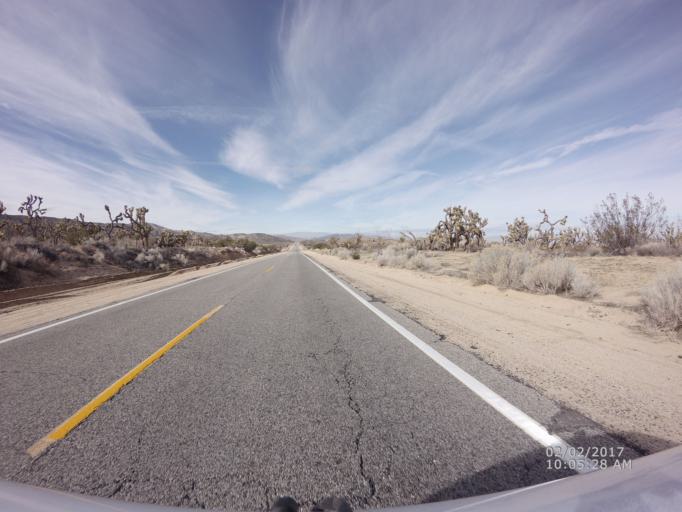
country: US
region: California
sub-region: Los Angeles County
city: Littlerock
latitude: 34.5066
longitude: -117.9884
